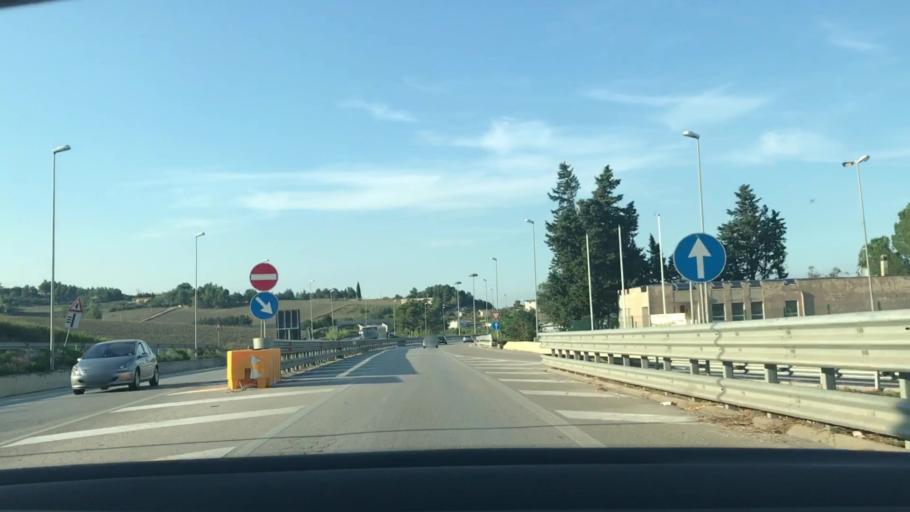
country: IT
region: Basilicate
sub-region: Provincia di Matera
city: Matera
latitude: 40.6874
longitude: 16.5902
